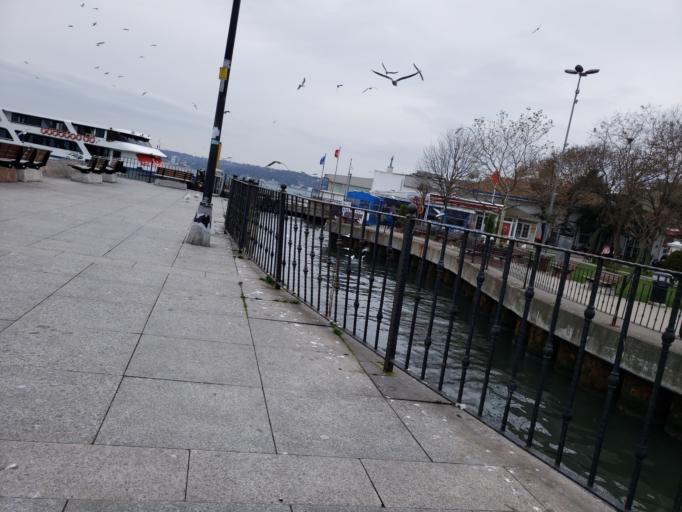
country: TR
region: Istanbul
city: Arikoey
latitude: 41.1669
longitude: 29.0577
